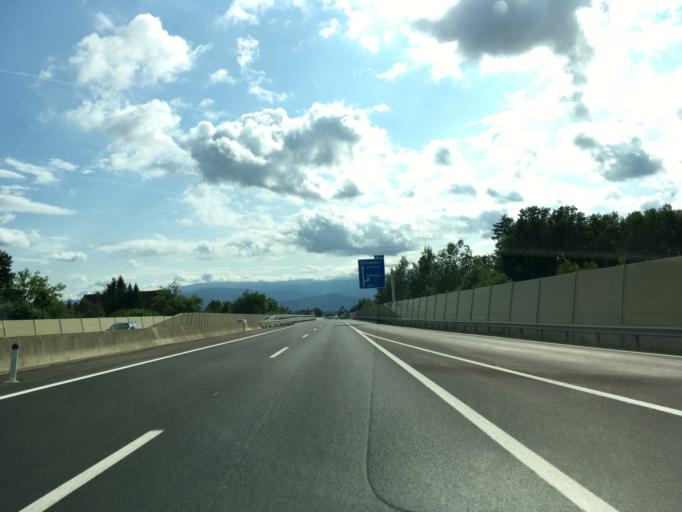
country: AT
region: Styria
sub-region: Politischer Bezirk Murtal
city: Spielberg bei Knittelfeld
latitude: 47.2158
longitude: 14.7977
